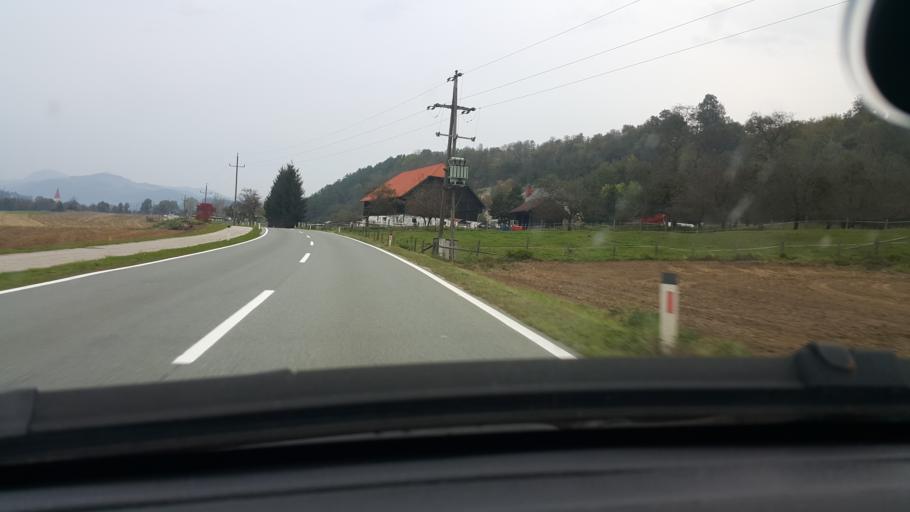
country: AT
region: Carinthia
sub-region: Politischer Bezirk Wolfsberg
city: Lavamund
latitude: 46.6291
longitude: 14.9673
